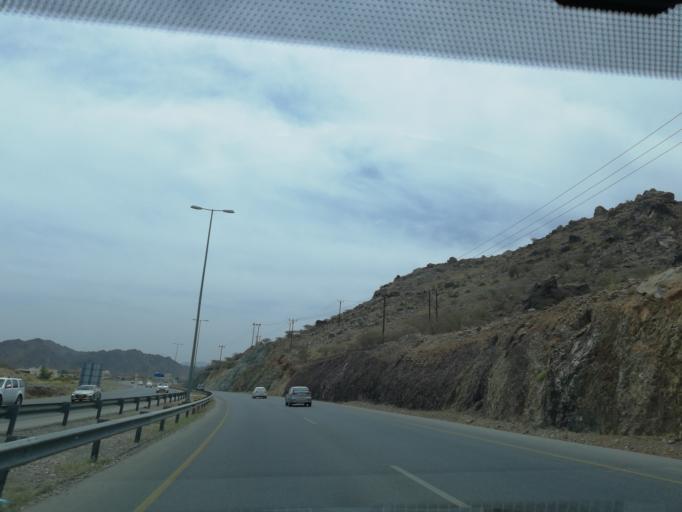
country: OM
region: Muhafazat ad Dakhiliyah
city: Izki
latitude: 23.1449
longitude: 57.8420
